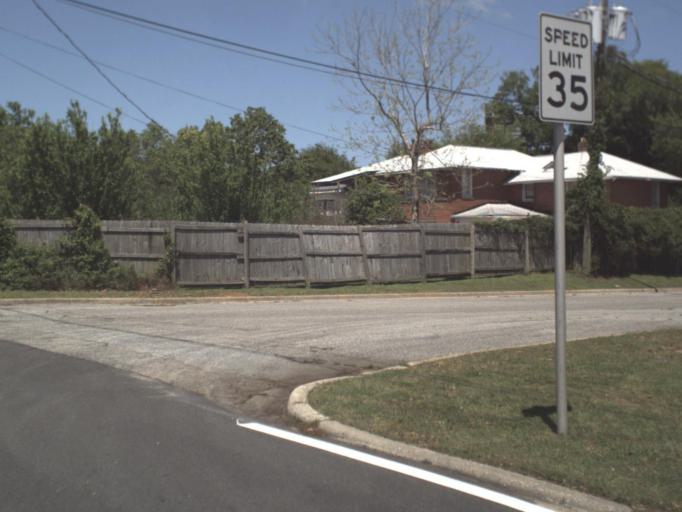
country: US
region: Florida
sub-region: Escambia County
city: West Pensacola
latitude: 30.4263
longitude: -87.2735
